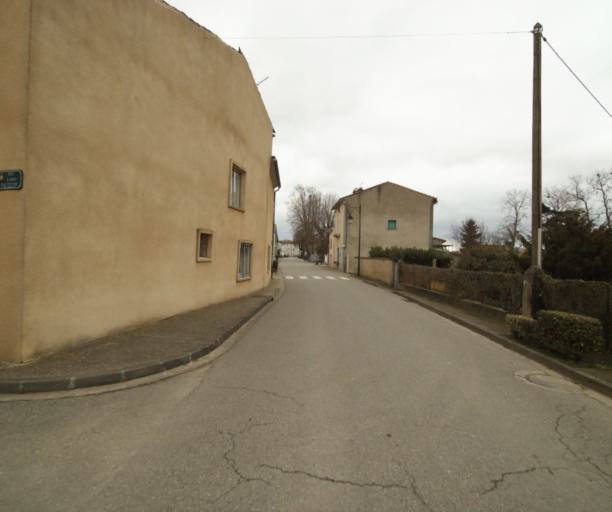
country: FR
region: Midi-Pyrenees
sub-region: Departement de l'Ariege
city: Pamiers
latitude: 43.1550
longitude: 1.6361
